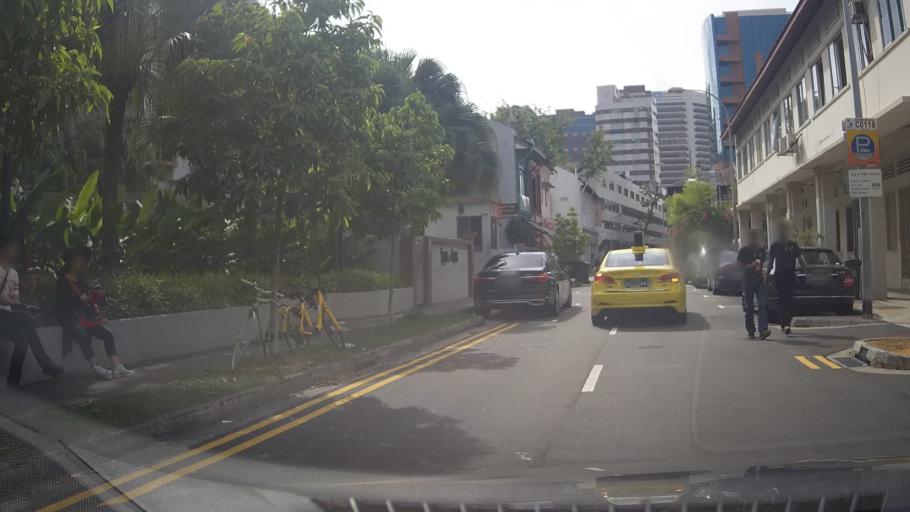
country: SG
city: Singapore
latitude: 1.3057
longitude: 103.9027
